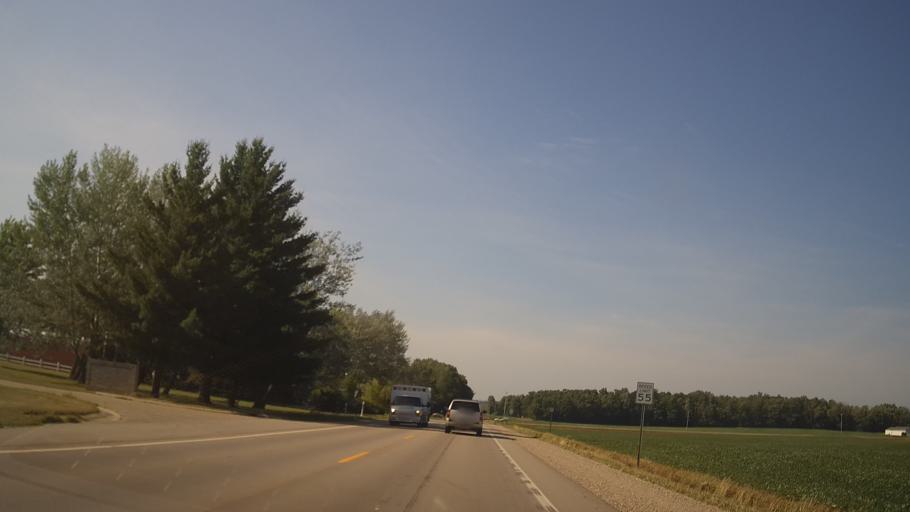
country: US
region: Michigan
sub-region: Ogemaw County
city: West Branch
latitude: 44.3098
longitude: -84.1258
